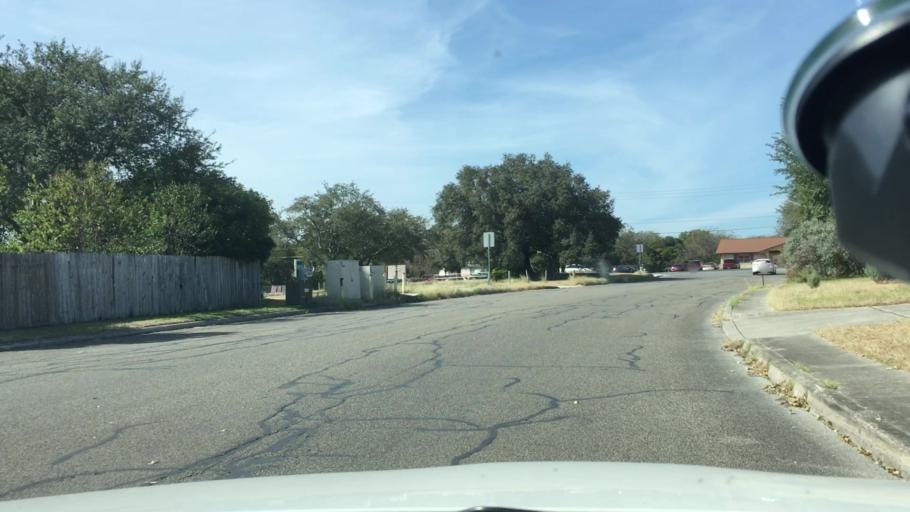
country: US
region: Texas
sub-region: Bexar County
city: Windcrest
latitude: 29.5722
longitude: -98.4172
